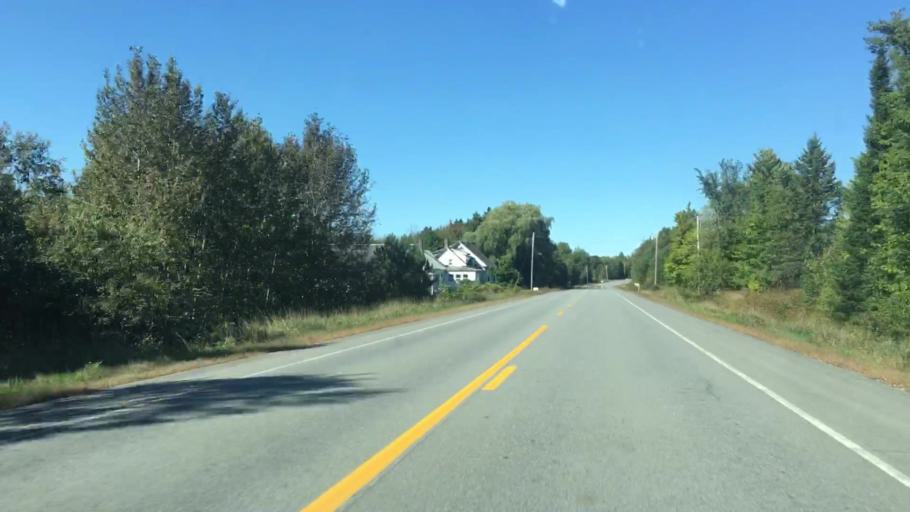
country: US
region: Maine
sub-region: Piscataquis County
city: Sangerville
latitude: 45.0664
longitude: -69.4586
